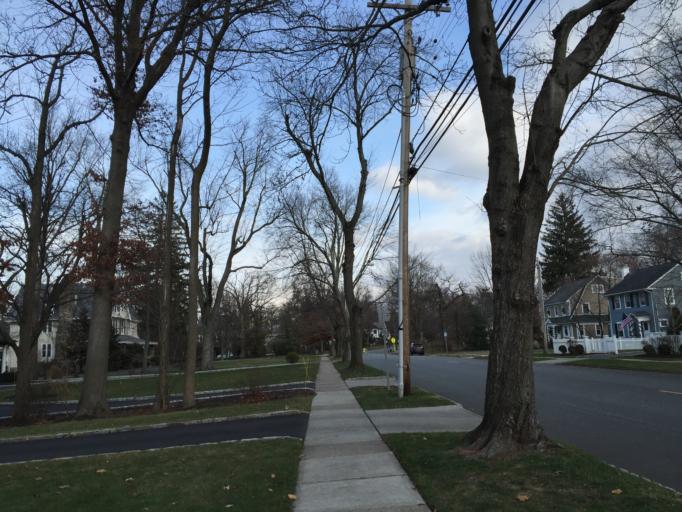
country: US
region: New Jersey
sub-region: Morris County
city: Chatham
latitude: 40.7207
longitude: -74.3766
